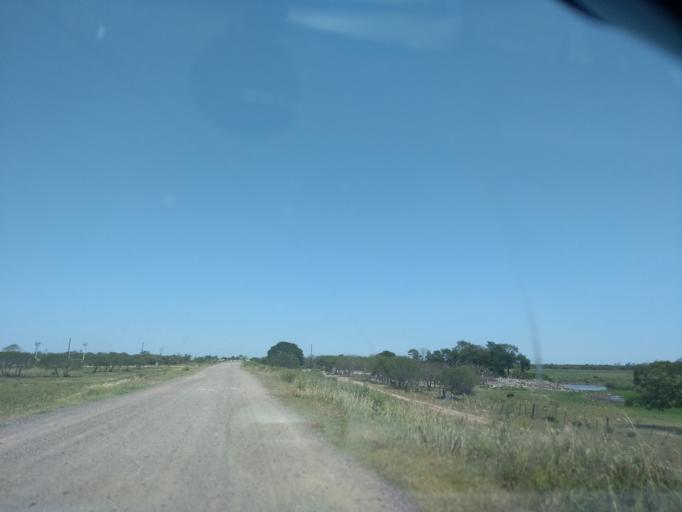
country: AR
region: Chaco
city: Resistencia
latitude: -27.4086
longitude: -58.9507
